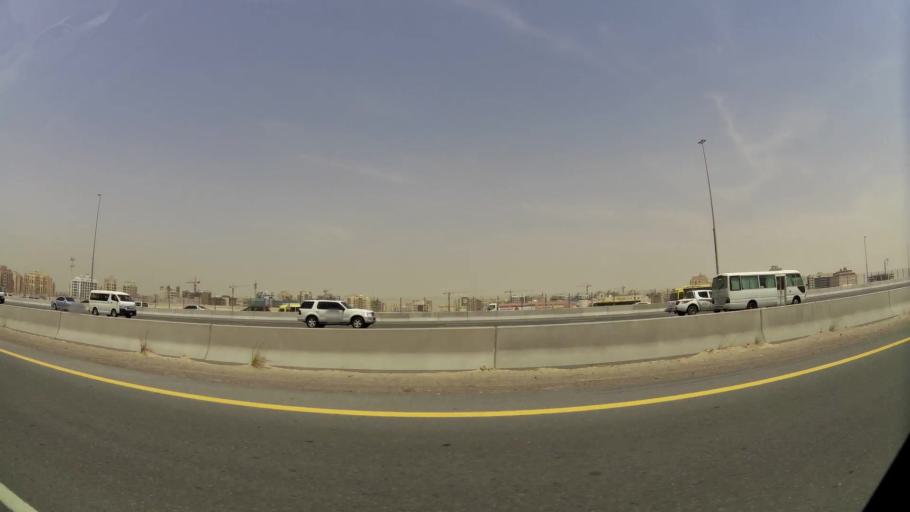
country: AE
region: Ash Shariqah
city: Sharjah
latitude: 25.1874
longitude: 55.3967
